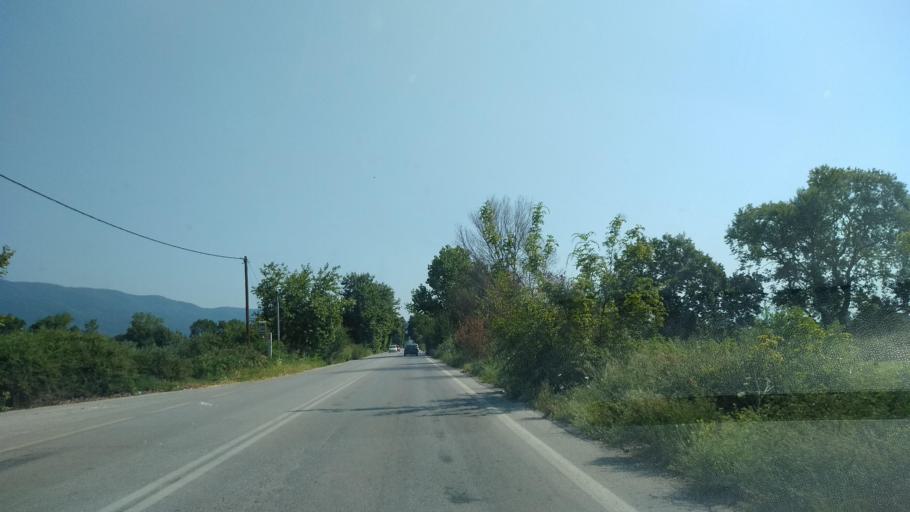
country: GR
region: Central Macedonia
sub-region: Nomos Thessalonikis
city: Nea Vrasna
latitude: 40.6948
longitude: 23.6857
